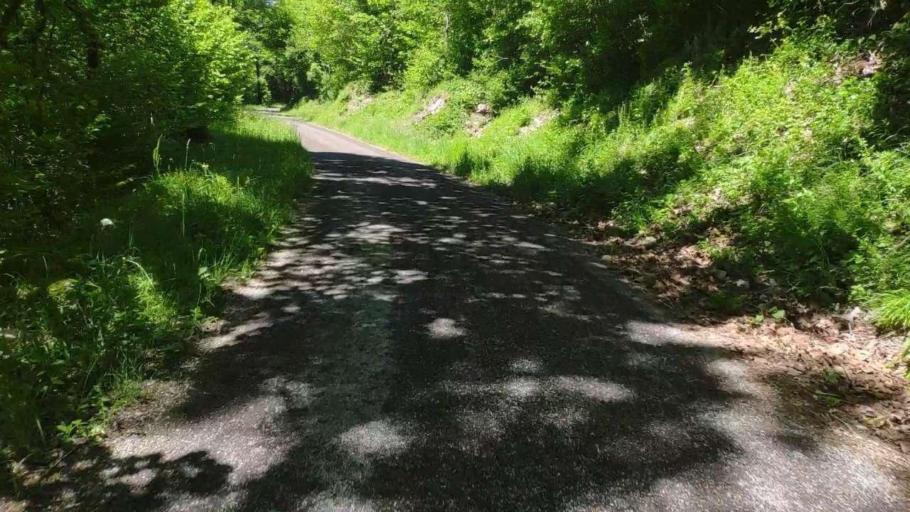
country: FR
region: Franche-Comte
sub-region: Departement du Jura
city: Poligny
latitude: 46.7485
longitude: 5.6828
